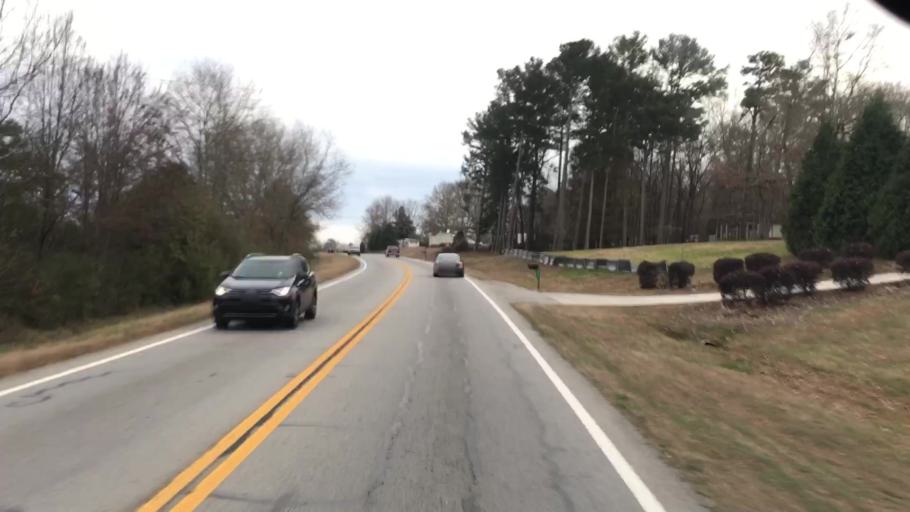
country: US
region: Georgia
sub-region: Barrow County
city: Winder
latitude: 34.0246
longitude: -83.7694
